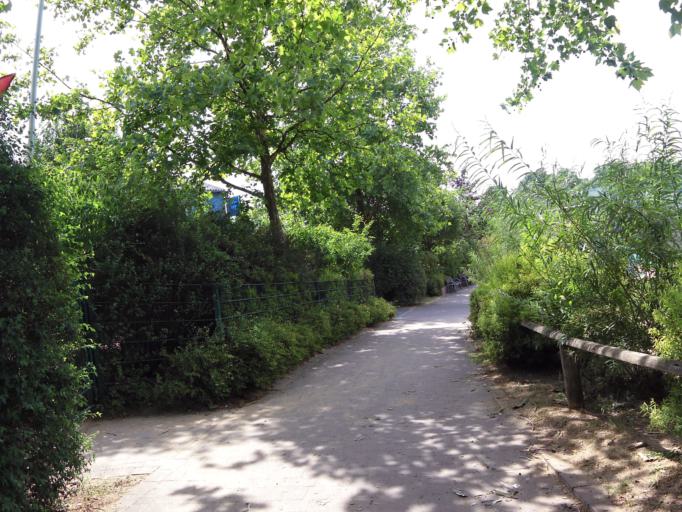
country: DE
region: Bavaria
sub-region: Regierungsbezirk Unterfranken
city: Randersacker
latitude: 49.7586
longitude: 9.9796
